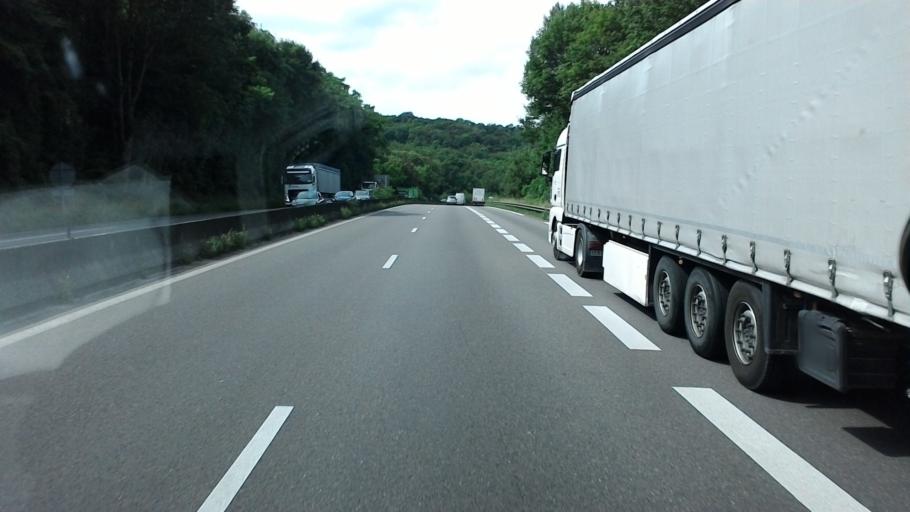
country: FR
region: Lorraine
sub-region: Departement de Meurthe-et-Moselle
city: Ludres
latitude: 48.6348
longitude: 6.1735
